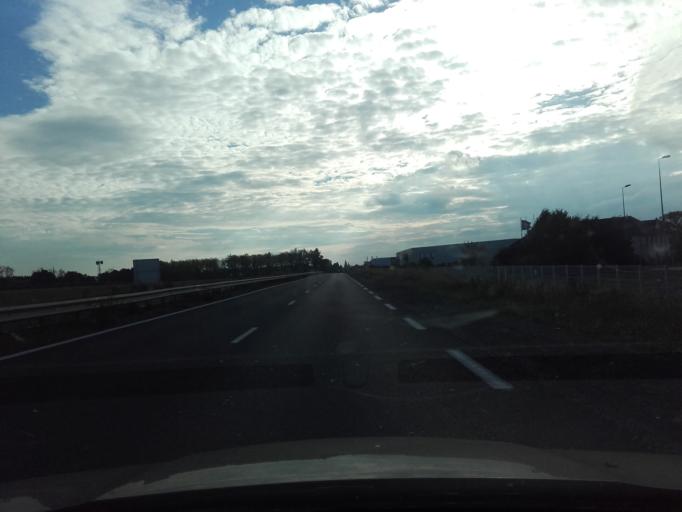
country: FR
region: Centre
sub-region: Departement d'Indre-et-Loire
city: Parcay-Meslay
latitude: 47.4461
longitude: 0.7239
